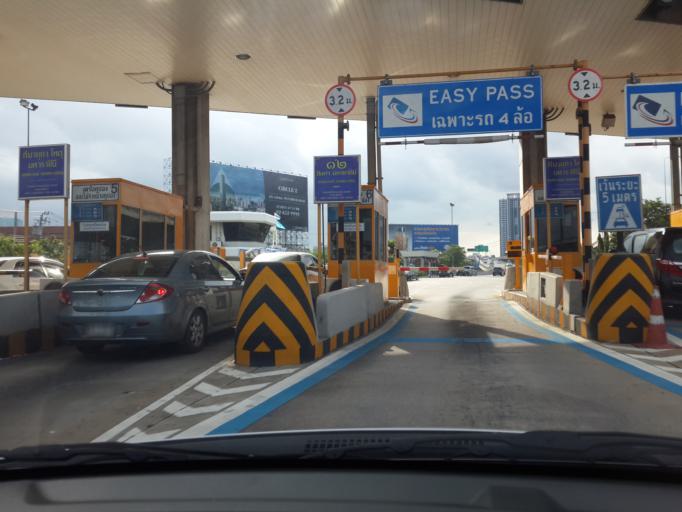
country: TH
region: Bangkok
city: Watthana
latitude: 13.7431
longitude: 100.6117
